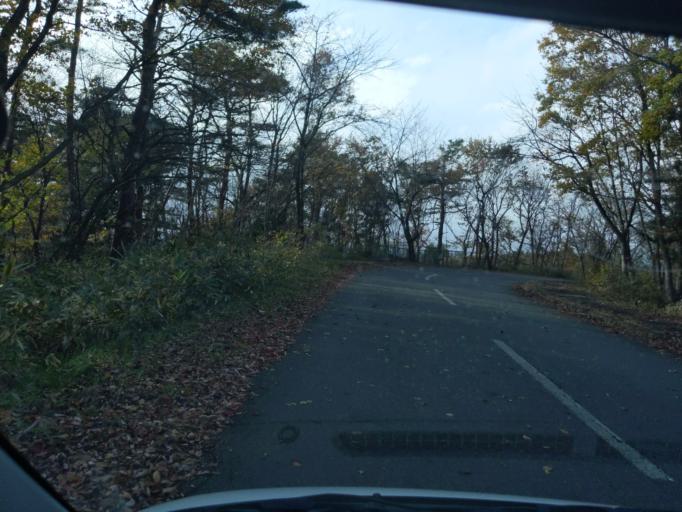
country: JP
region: Iwate
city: Ichinoseki
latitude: 39.0222
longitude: 141.0995
